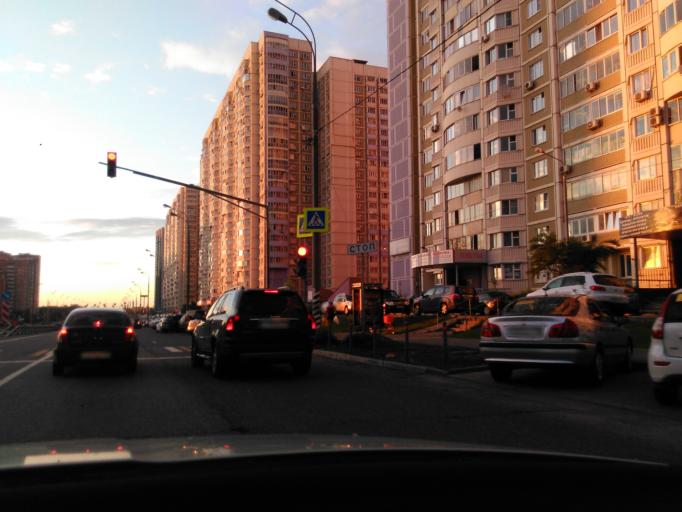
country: RU
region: Moscow
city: Khimki
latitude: 55.9048
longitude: 37.3899
